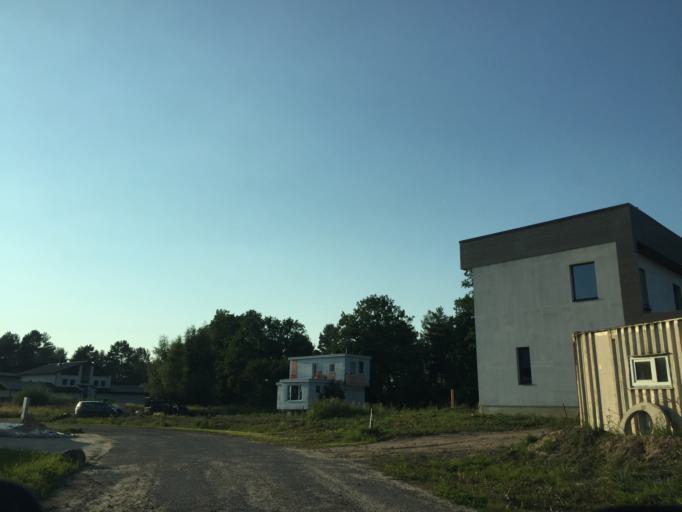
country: LV
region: Garkalne
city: Garkalne
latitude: 56.9799
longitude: 24.3816
